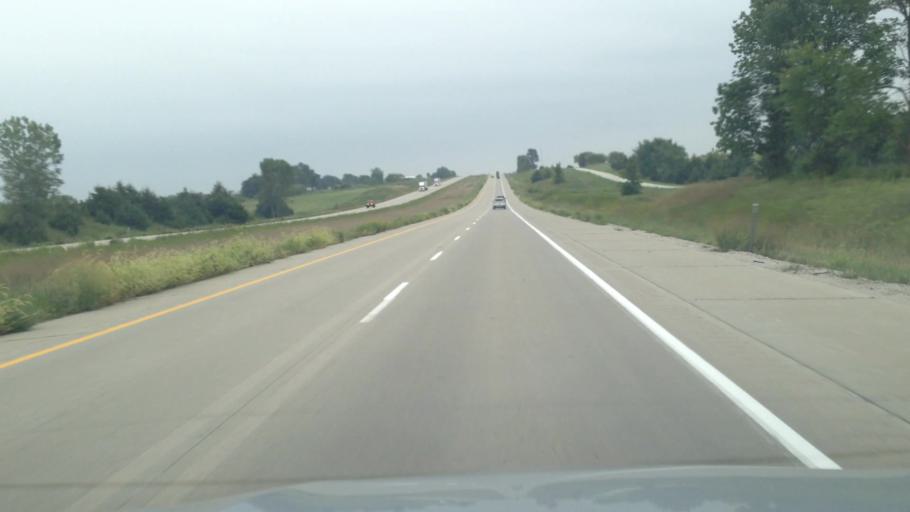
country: US
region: Iowa
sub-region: Decatur County
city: Leon
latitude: 40.7898
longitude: -93.8351
